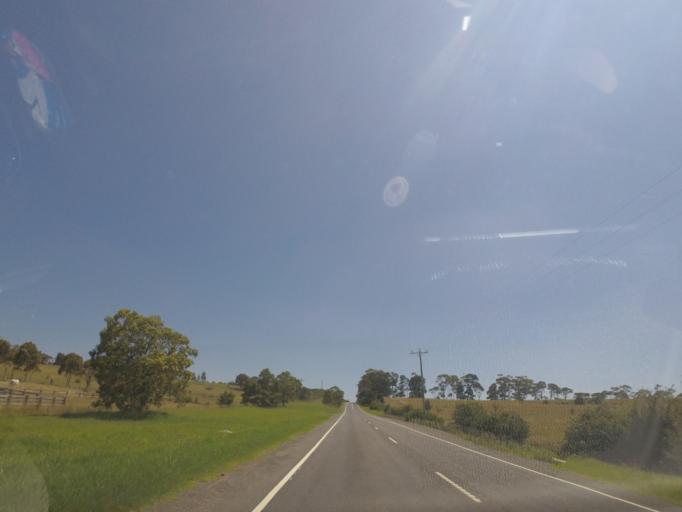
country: AU
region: Victoria
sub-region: Hume
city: Greenvale
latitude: -37.5991
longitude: 144.8417
